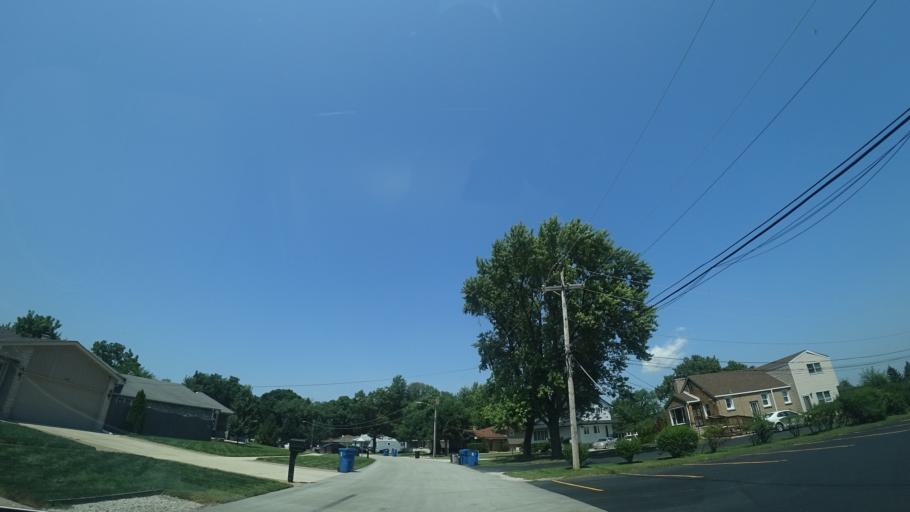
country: US
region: Illinois
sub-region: Cook County
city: Alsip
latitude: 41.6840
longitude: -87.7467
